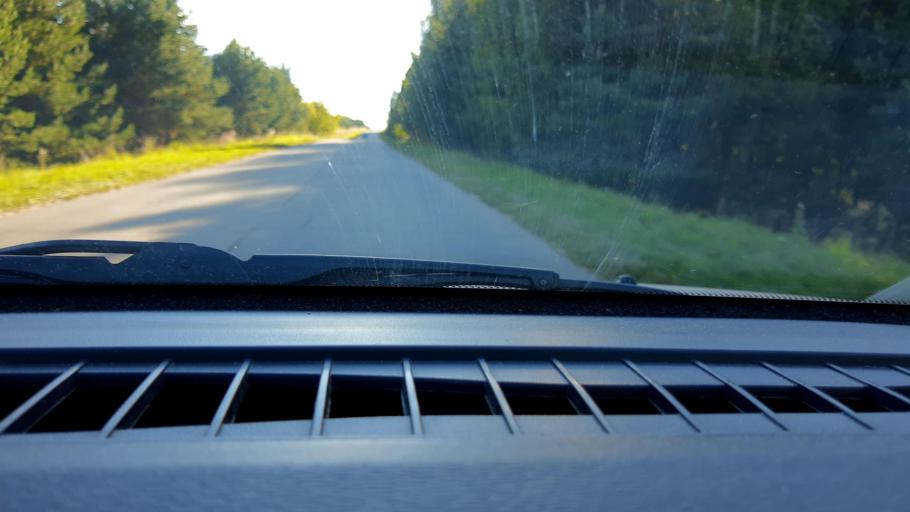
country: RU
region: Nizjnij Novgorod
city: Surovatikha
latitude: 55.9418
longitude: 43.9059
